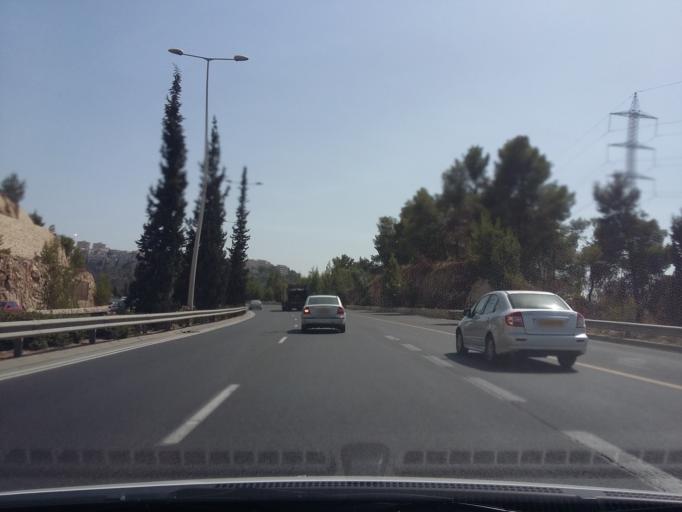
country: IL
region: Jerusalem
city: West Jerusalem
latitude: 31.8056
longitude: 35.2058
